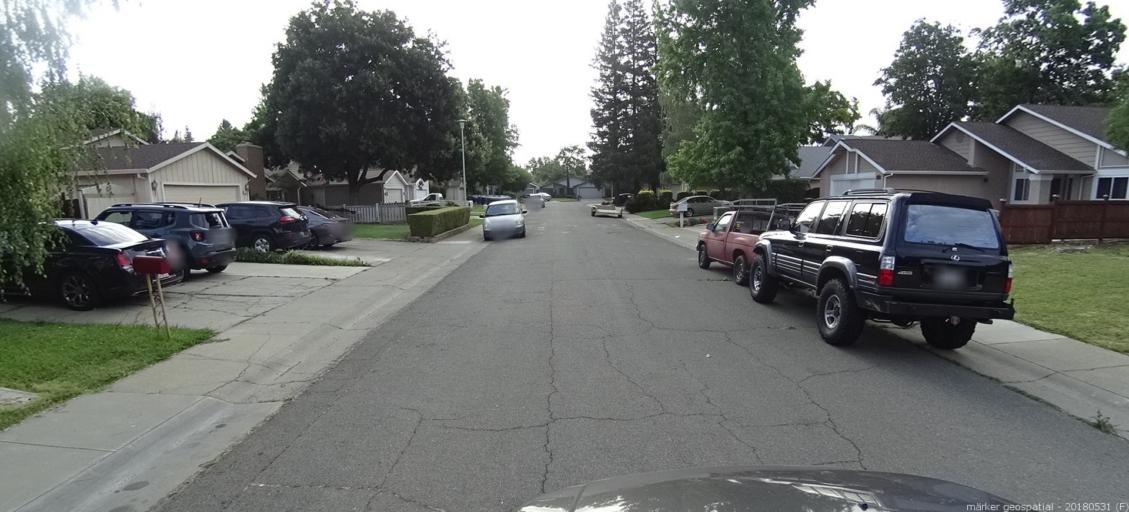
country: US
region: California
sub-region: Sacramento County
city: Sacramento
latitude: 38.6255
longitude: -121.4926
